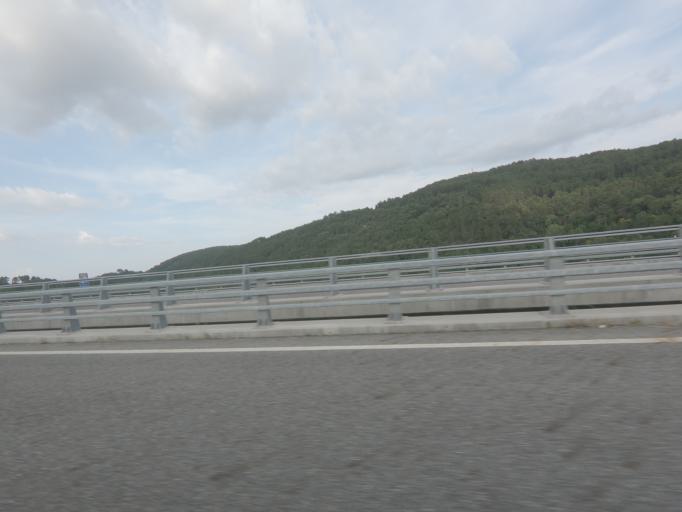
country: PT
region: Vila Real
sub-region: Boticas
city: Boticas
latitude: 41.6816
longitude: -7.5665
